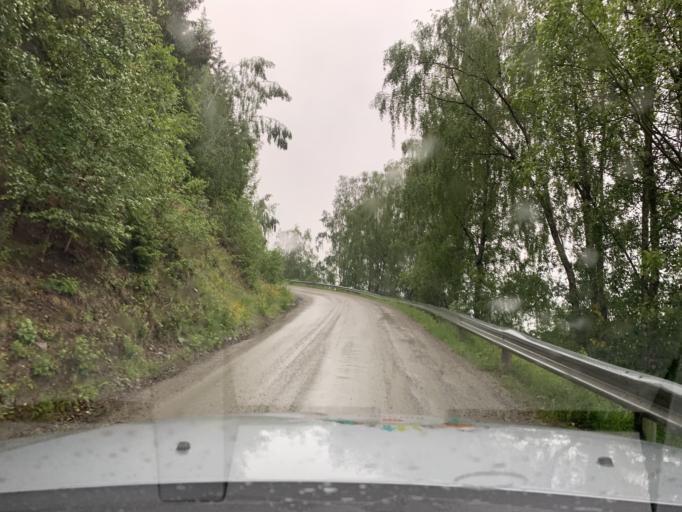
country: NO
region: Oppland
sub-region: Oyer
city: Tretten
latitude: 61.3917
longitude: 10.2487
